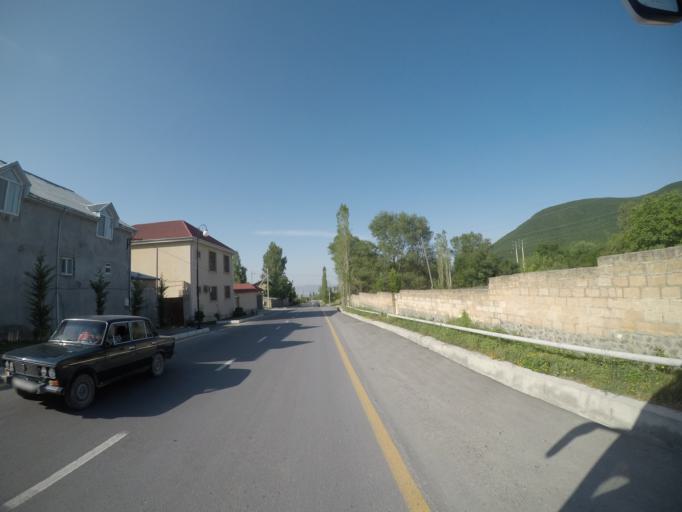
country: AZ
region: Shaki City
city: Sheki
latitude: 41.2245
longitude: 47.1722
